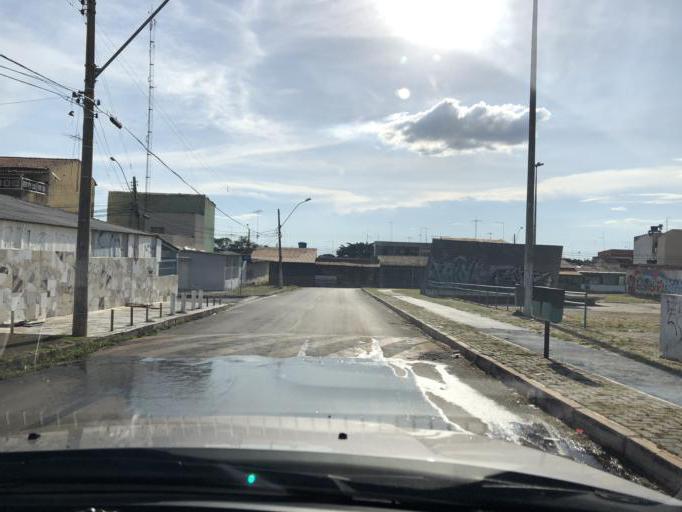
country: BR
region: Federal District
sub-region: Brasilia
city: Brasilia
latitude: -15.8104
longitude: -48.1293
